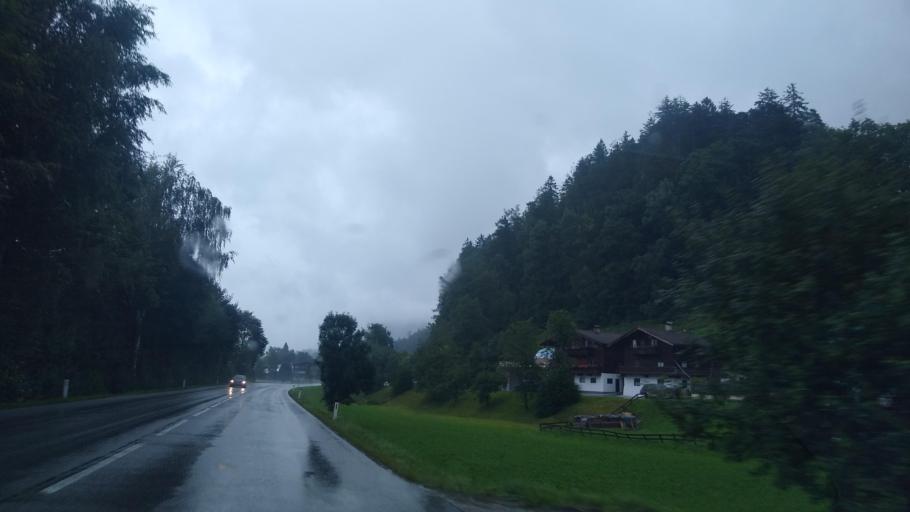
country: AT
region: Tyrol
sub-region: Politischer Bezirk Kufstein
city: Munster
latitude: 47.4121
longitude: 11.8503
